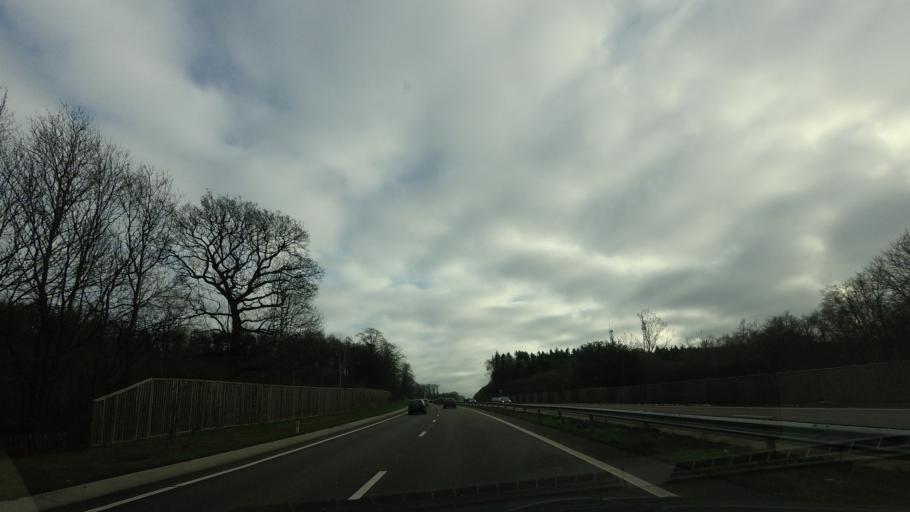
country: GB
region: England
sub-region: Kent
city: Tonbridge
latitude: 51.1755
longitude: 0.2951
